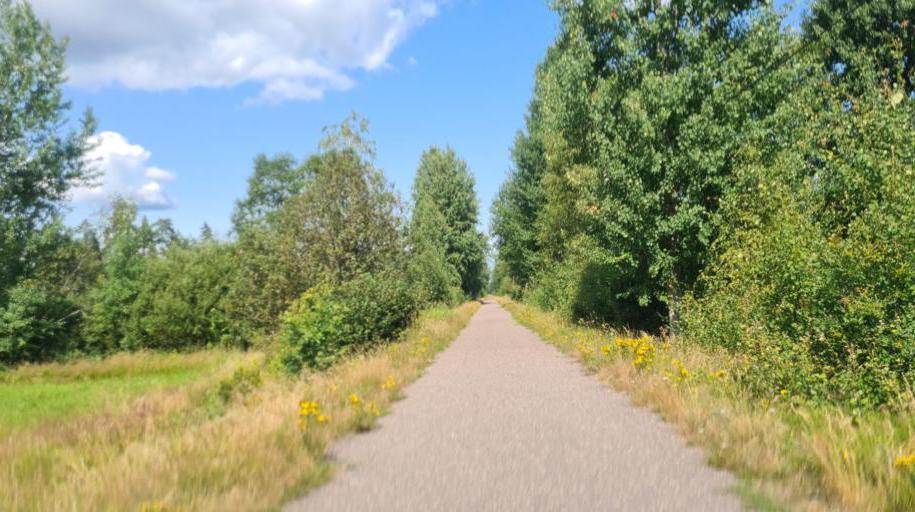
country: SE
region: Kronoberg
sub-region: Ljungby Kommun
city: Ljungby
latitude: 56.8477
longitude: 13.9658
